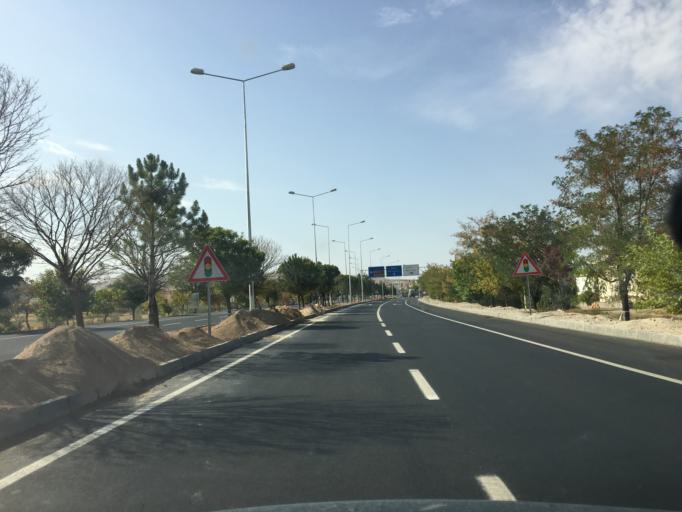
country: TR
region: Nevsehir
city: Avanos
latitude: 38.7036
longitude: 34.8460
